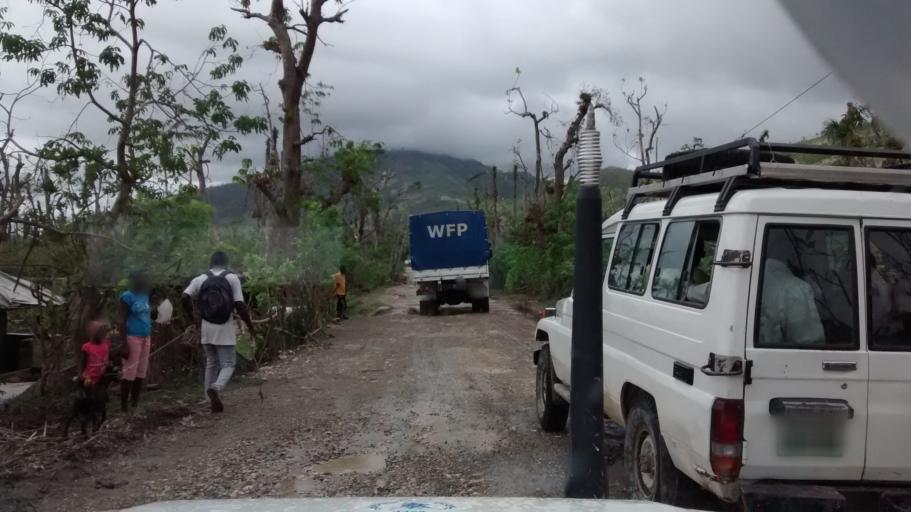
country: HT
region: Grandans
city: Moron
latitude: 18.5988
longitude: -74.1911
